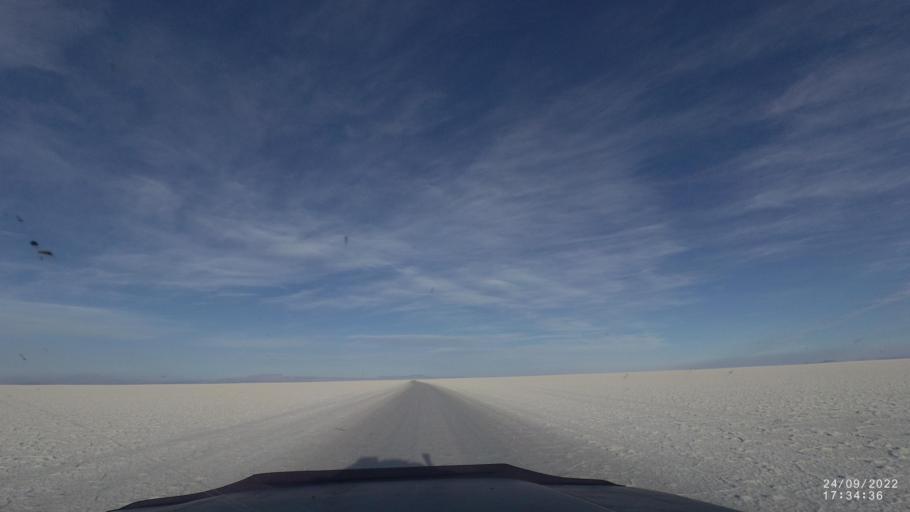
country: BO
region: Potosi
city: Colchani
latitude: -20.3214
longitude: -67.2780
